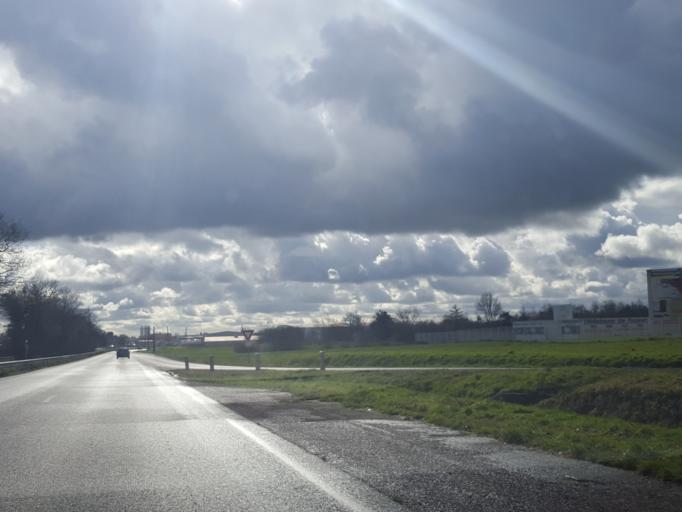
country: FR
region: Pays de la Loire
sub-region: Departement de la Vendee
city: Mouilleron-le-Captif
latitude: 46.7432
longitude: -1.4305
